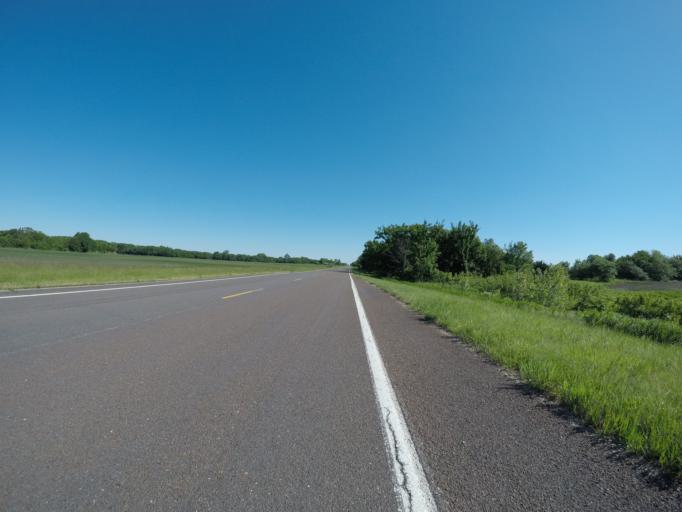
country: US
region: Kansas
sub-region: Osage County
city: Osage City
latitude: 38.7146
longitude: -96.0940
